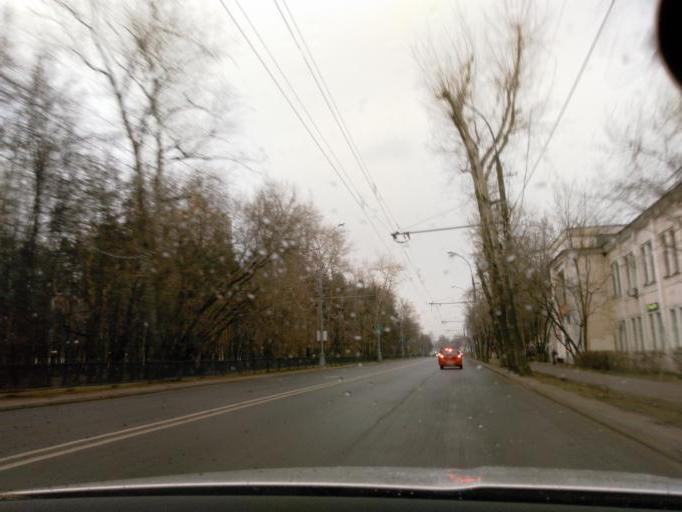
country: RU
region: Moskovskaya
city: Levoberezhnyy
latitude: 55.8396
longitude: 37.4546
